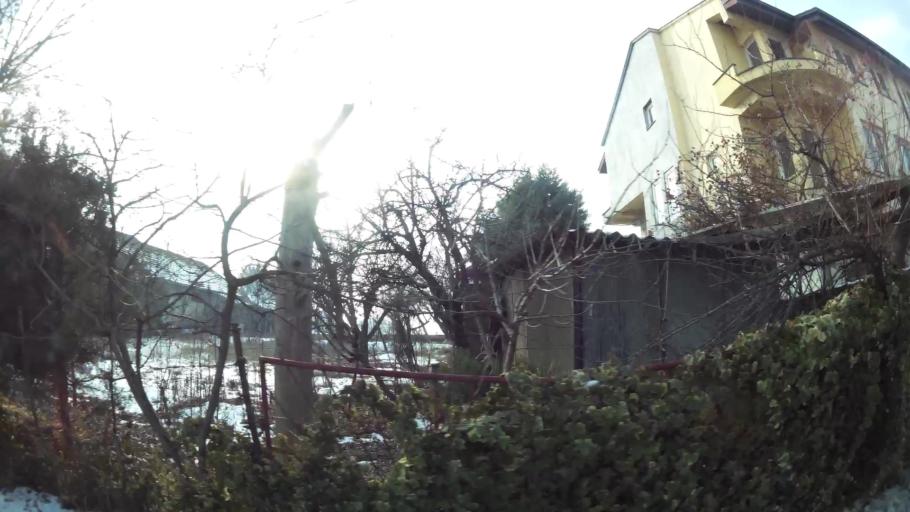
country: MK
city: Creshevo
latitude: 42.0089
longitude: 21.4979
